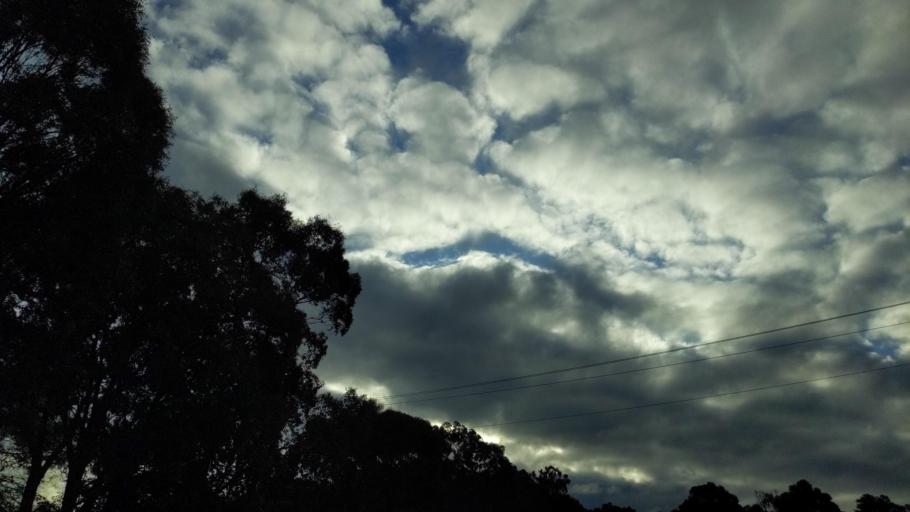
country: AU
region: New South Wales
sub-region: Wagga Wagga
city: Wagga Wagga
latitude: -35.0686
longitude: 147.3789
